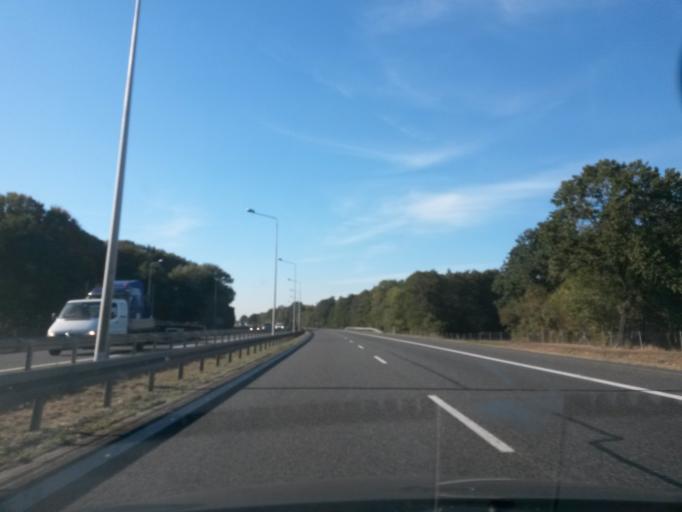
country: PL
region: Opole Voivodeship
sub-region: Powiat brzeski
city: Grodkow
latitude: 50.7659
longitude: 17.4115
